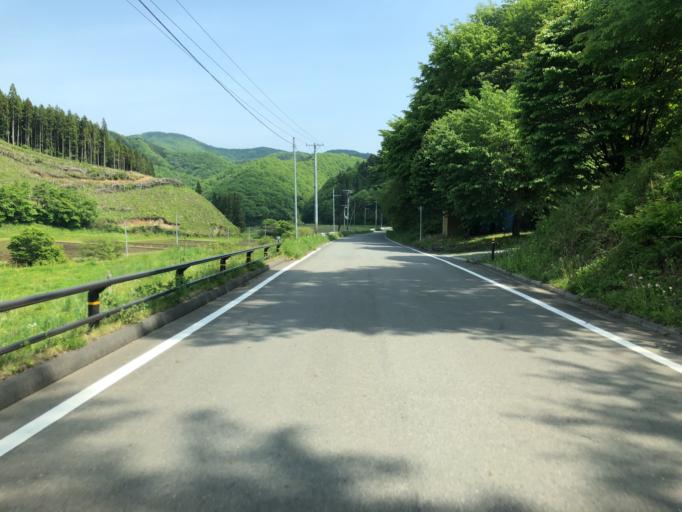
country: JP
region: Fukushima
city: Ishikawa
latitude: 36.9967
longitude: 140.6131
